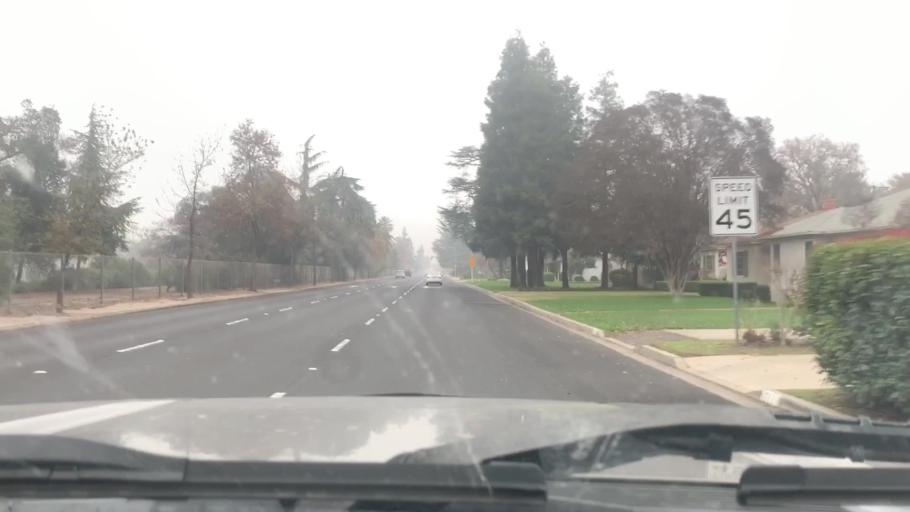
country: US
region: California
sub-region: Tulare County
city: Visalia
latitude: 36.3265
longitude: -119.3089
